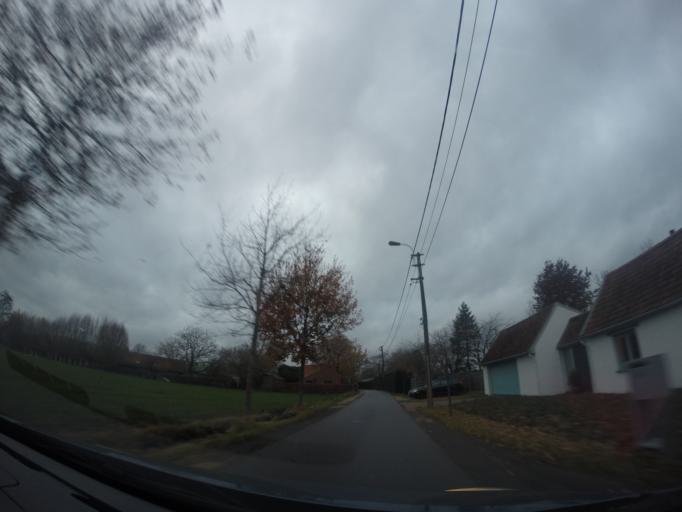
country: BE
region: Flanders
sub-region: Provincie Oost-Vlaanderen
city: Nevele
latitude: 51.0718
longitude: 3.5137
